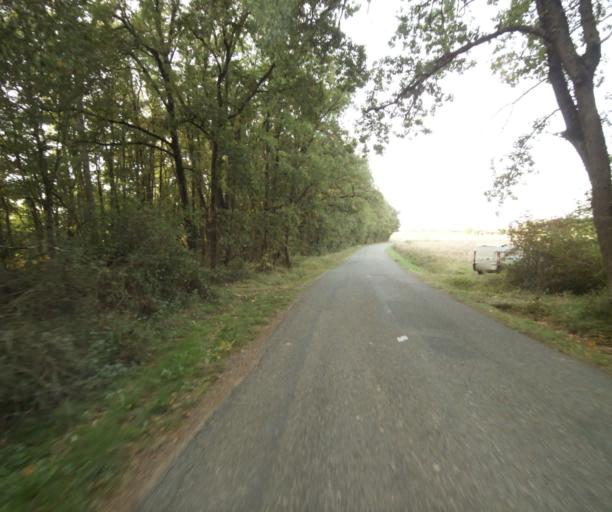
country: FR
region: Midi-Pyrenees
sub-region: Departement du Tarn-et-Garonne
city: Campsas
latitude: 43.8722
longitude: 1.3414
